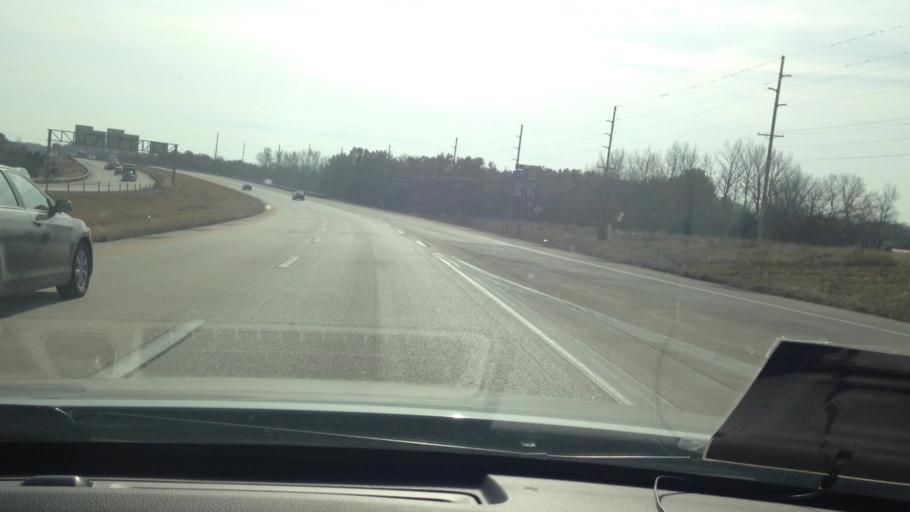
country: US
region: Missouri
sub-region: Cass County
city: Harrisonville
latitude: 38.6499
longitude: -94.3651
